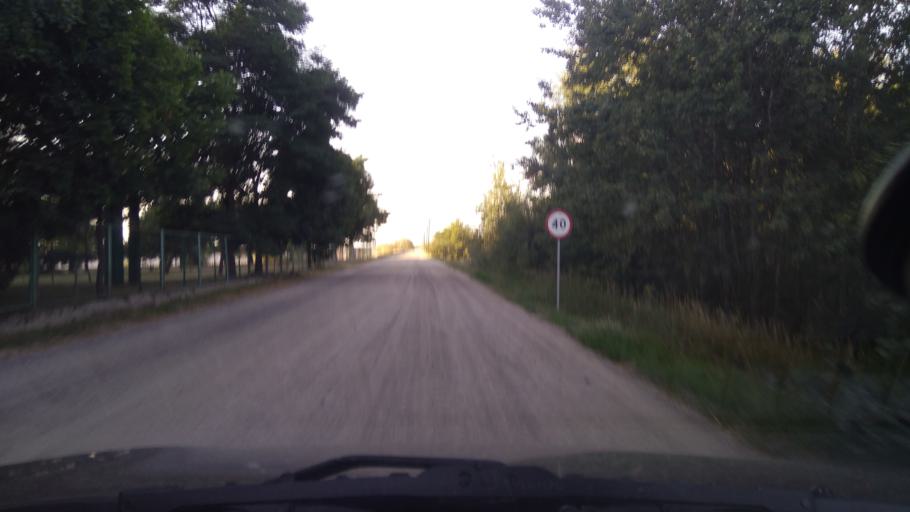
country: BY
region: Brest
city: Byaroza
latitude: 52.6018
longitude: 24.8774
